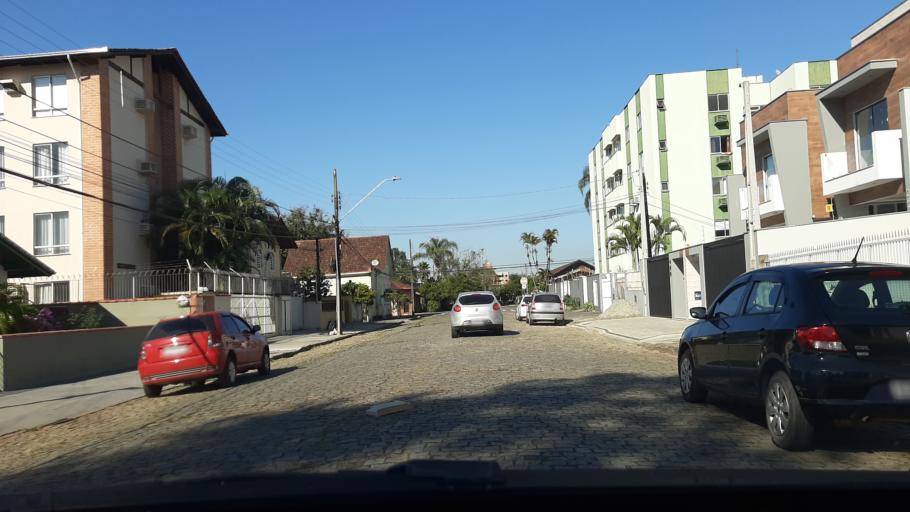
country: BR
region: Santa Catarina
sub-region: Joinville
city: Joinville
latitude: -26.3135
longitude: -48.8377
